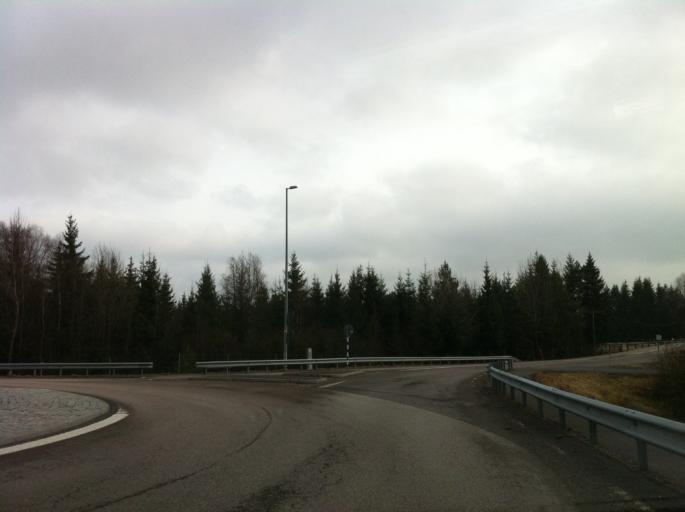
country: SE
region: Vaestra Goetaland
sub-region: Boras Kommun
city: Dalsjofors
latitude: 57.7461
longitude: 13.1067
